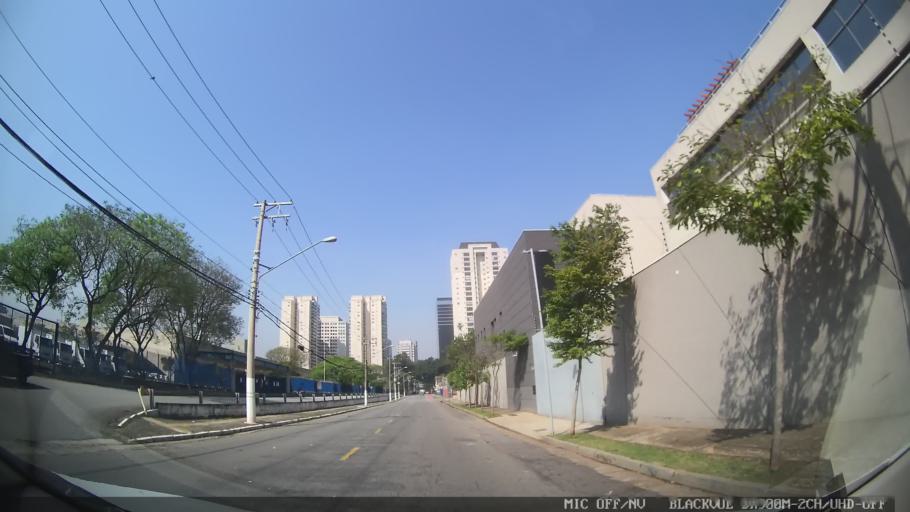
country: BR
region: Sao Paulo
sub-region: Sao Paulo
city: Sao Paulo
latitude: -23.5180
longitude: -46.6616
